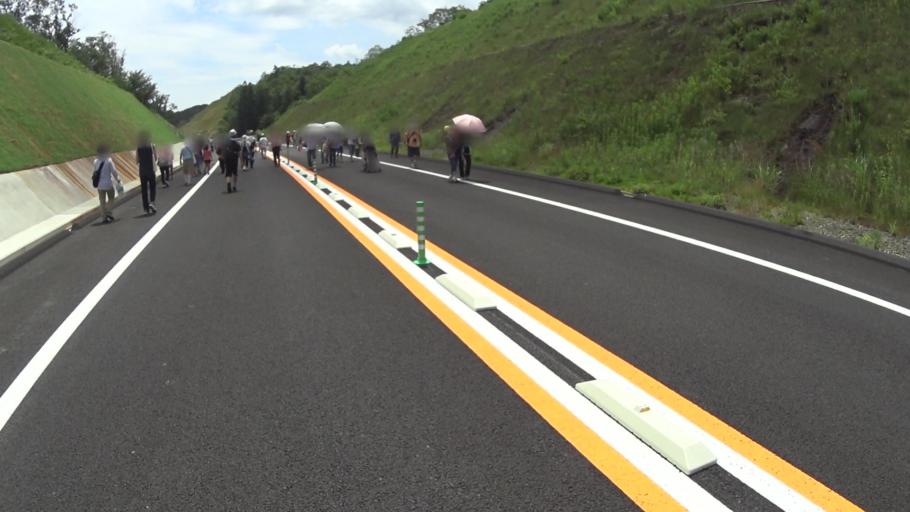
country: JP
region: Kyoto
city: Ayabe
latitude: 35.1697
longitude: 135.3725
